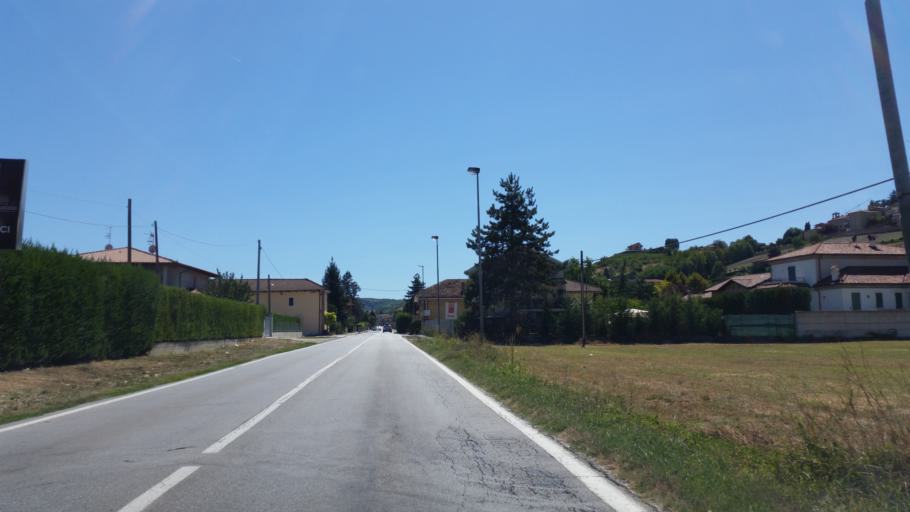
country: IT
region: Piedmont
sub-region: Provincia di Cuneo
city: Neive-Borgonovo
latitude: 44.7293
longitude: 8.1228
